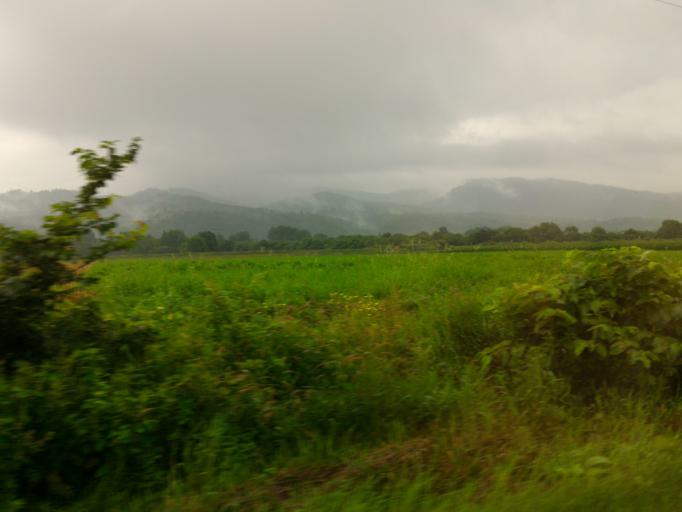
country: JP
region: Hokkaido
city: Nayoro
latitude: 44.5793
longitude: 142.3100
